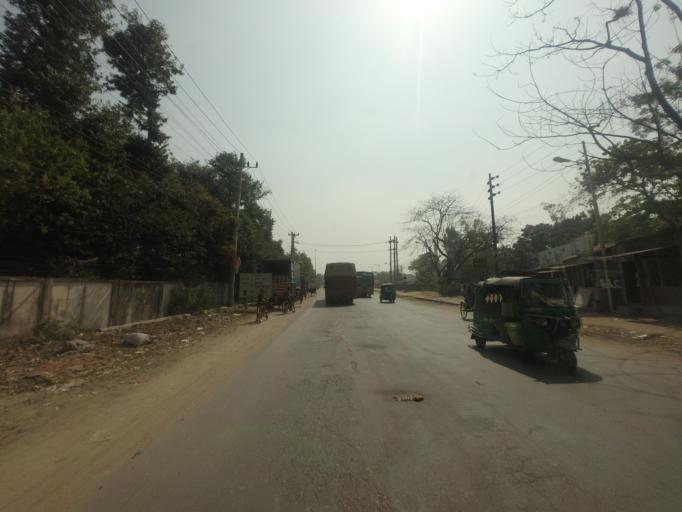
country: BD
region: Dhaka
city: Bhairab Bazar
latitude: 24.0543
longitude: 90.9868
